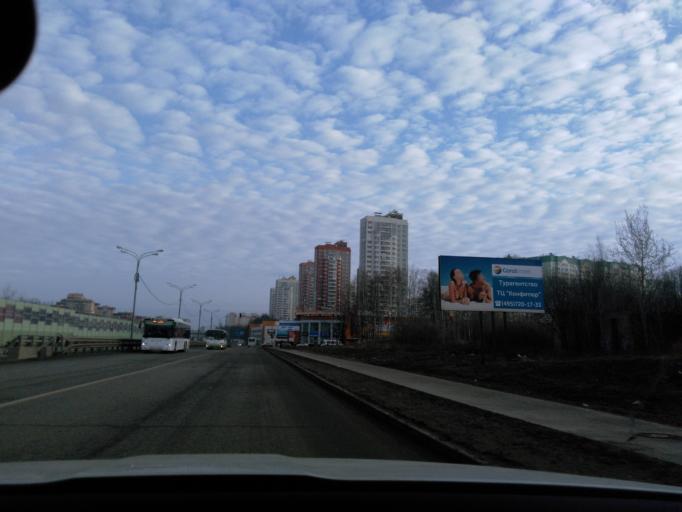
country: RU
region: Moskovskaya
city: Dolgoprudnyy
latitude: 55.9289
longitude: 37.4931
